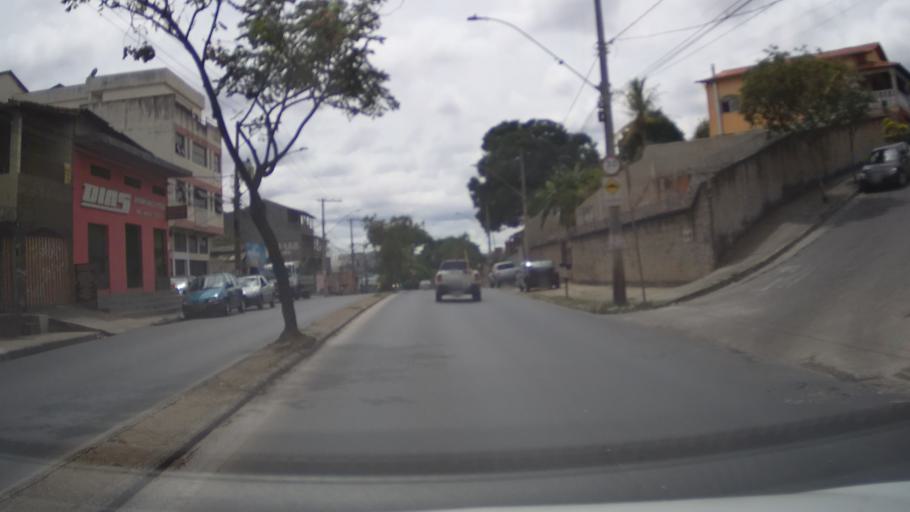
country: BR
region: Minas Gerais
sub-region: Ribeirao Das Neves
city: Ribeirao das Neves
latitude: -19.8035
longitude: -43.9872
